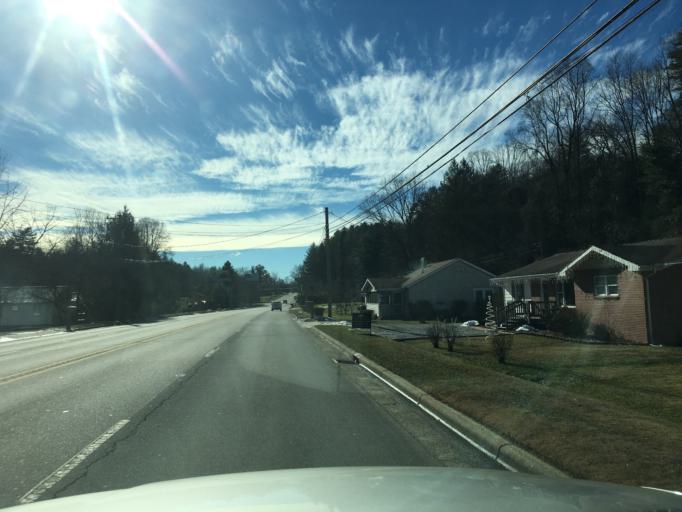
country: US
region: North Carolina
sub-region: Transylvania County
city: Brevard
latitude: 35.2828
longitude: -82.6929
